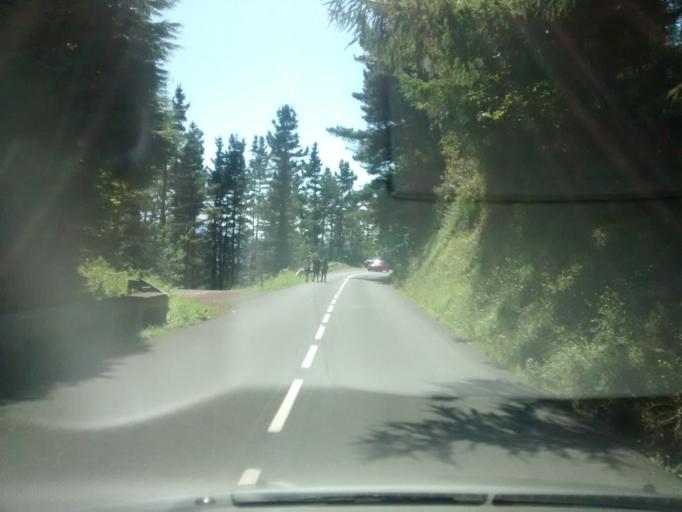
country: ES
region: Basque Country
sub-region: Provincia de Guipuzcoa
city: Eibar
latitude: 43.2116
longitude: -2.4612
